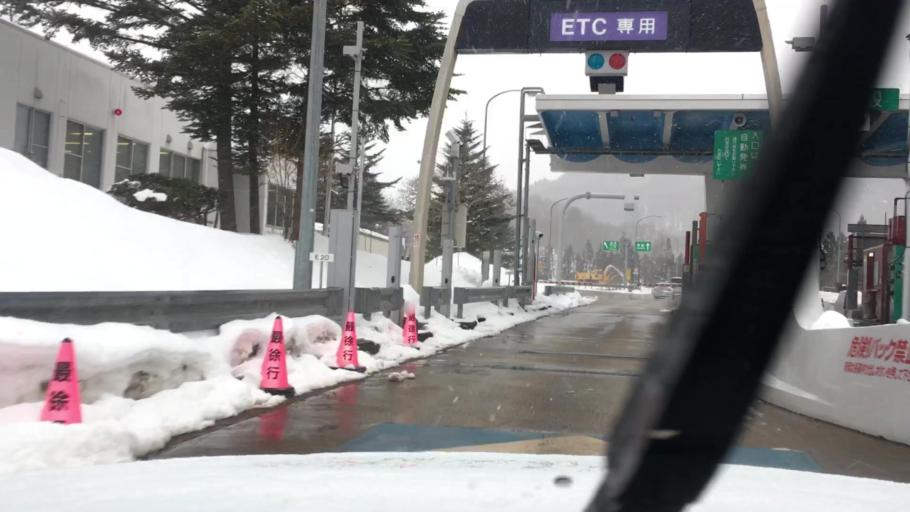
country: JP
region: Iwate
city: Ichinohe
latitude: 40.1103
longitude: 141.0507
